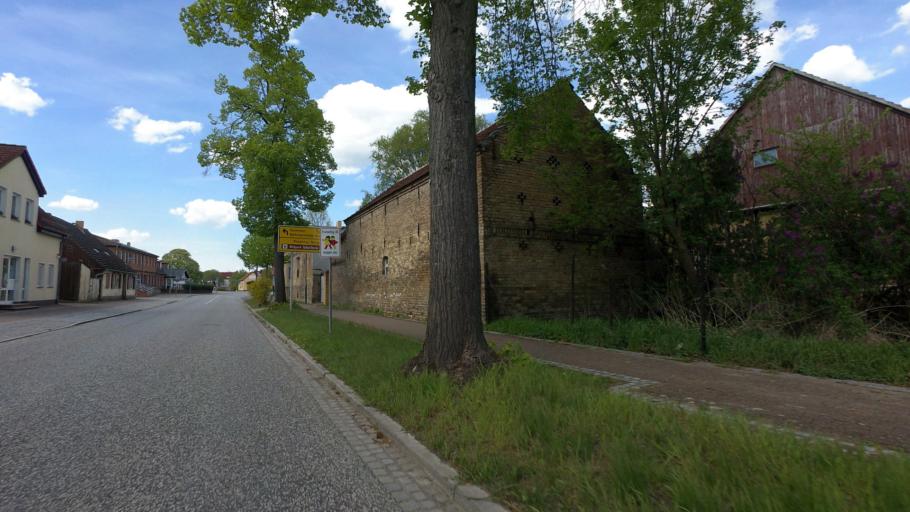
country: DE
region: Brandenburg
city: Marienwerder
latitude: 52.9061
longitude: 13.5325
